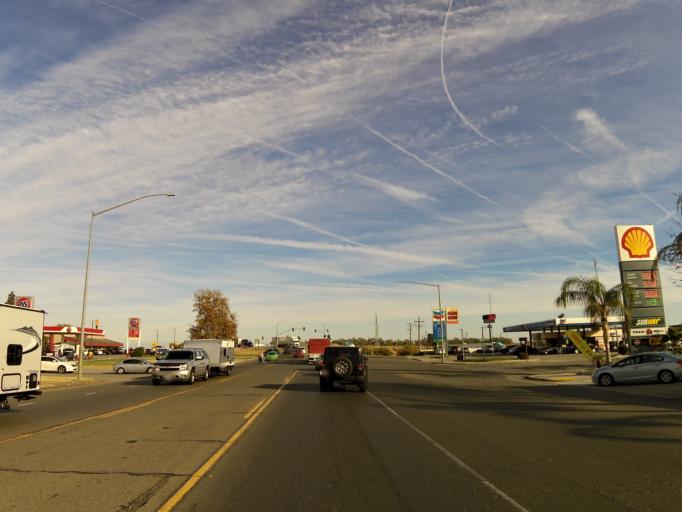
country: US
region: California
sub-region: Kern County
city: Lost Hills
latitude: 35.6161
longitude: -119.6581
